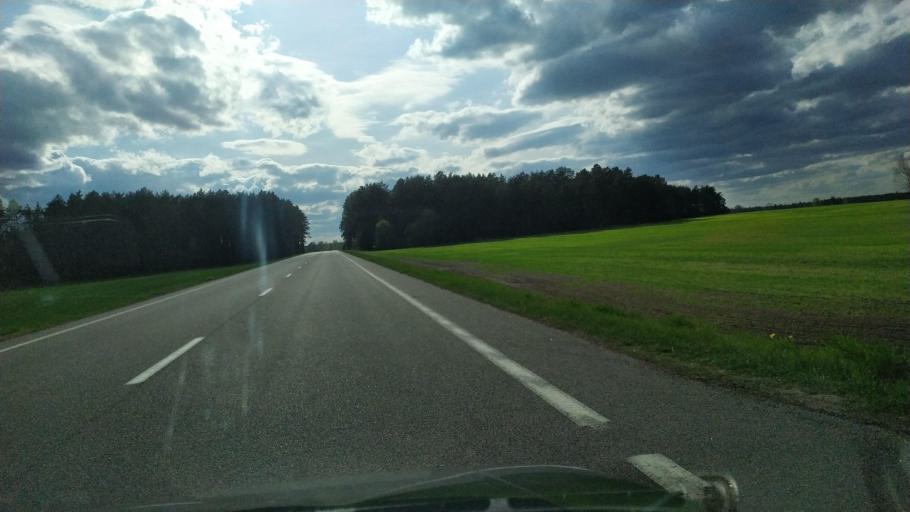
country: BY
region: Brest
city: Pruzhany
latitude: 52.6968
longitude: 24.2365
